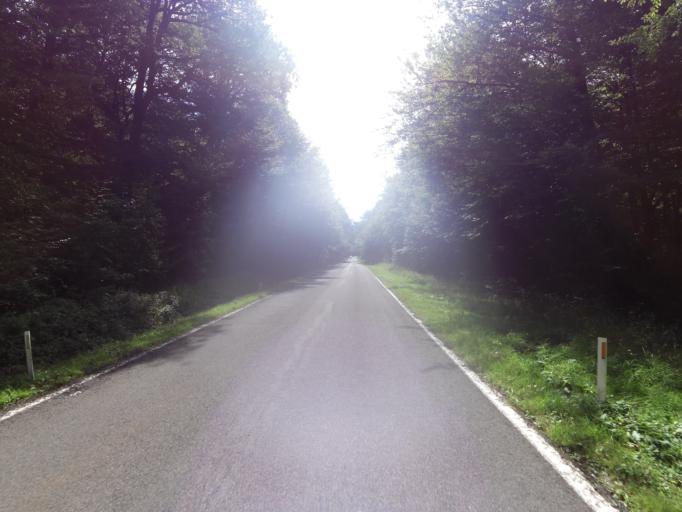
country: BE
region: Wallonia
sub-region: Province du Luxembourg
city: Saint-Hubert
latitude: 50.0619
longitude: 5.3457
